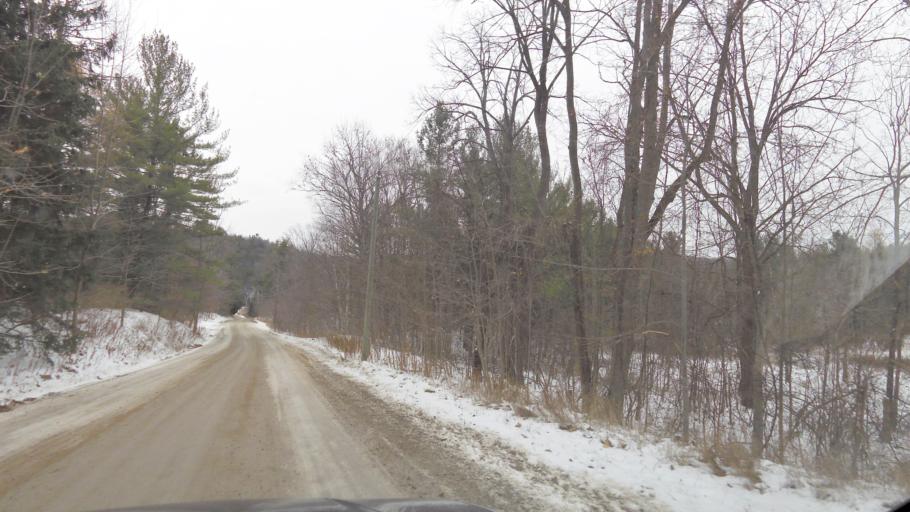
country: CA
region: Ontario
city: Vaughan
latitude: 43.9473
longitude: -79.6119
